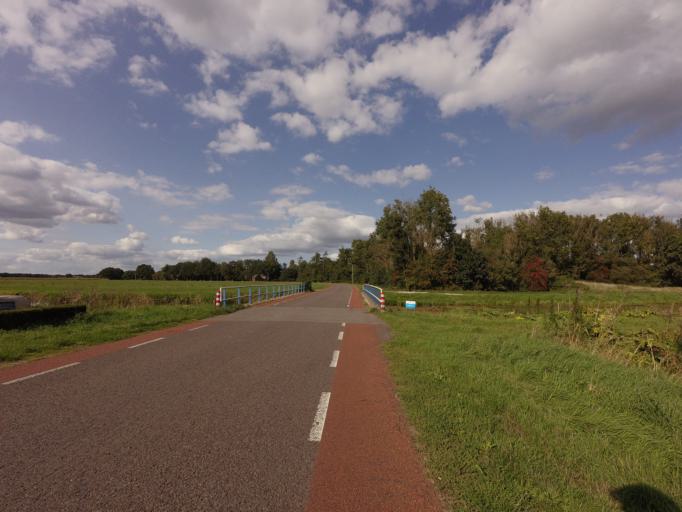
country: NL
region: Drenthe
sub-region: Gemeente Westerveld
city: Dwingeloo
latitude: 52.8439
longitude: 6.3992
